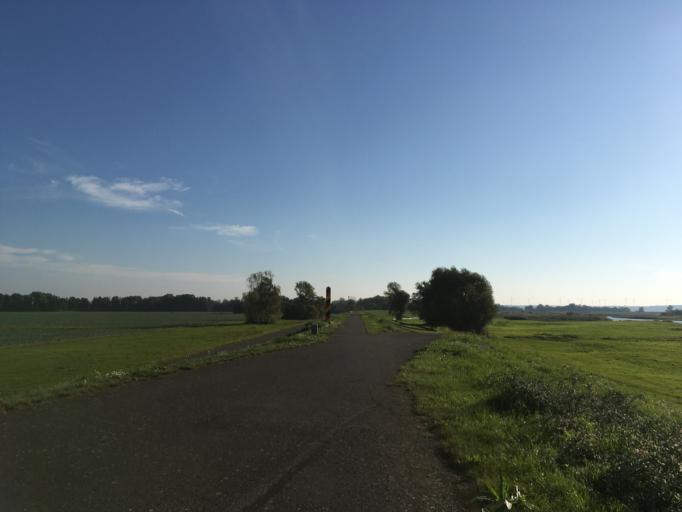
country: DE
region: Brandenburg
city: Lebus
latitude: 52.4430
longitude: 14.5617
